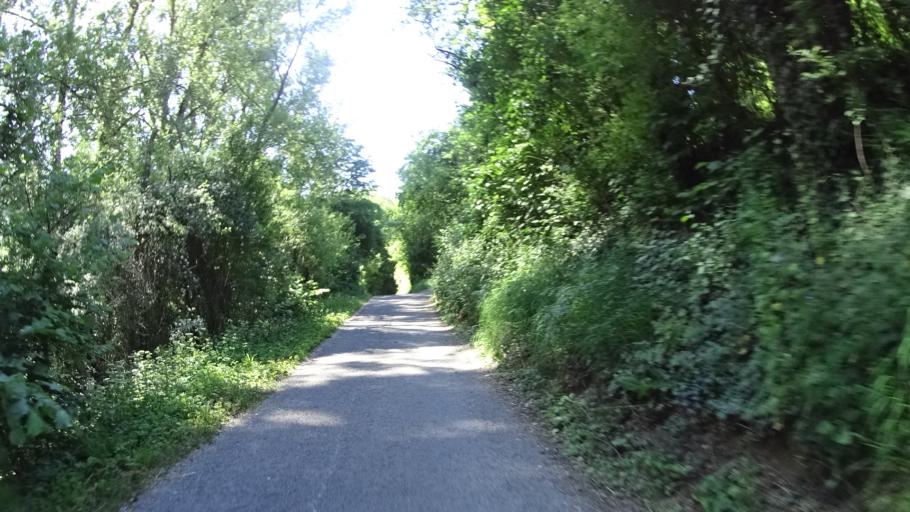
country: DE
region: Baden-Wuerttemberg
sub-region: Regierungsbezirk Stuttgart
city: Igersheim
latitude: 49.4875
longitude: 9.8144
